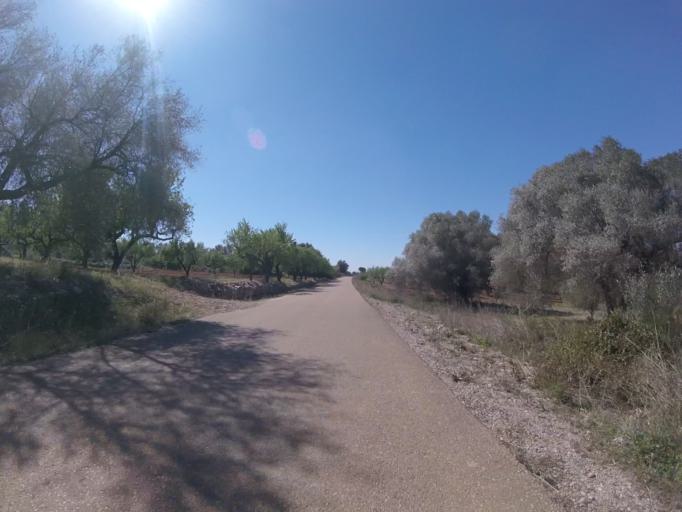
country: ES
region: Valencia
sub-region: Provincia de Castello
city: Cuevas de Vinroma
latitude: 40.3977
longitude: 0.1657
